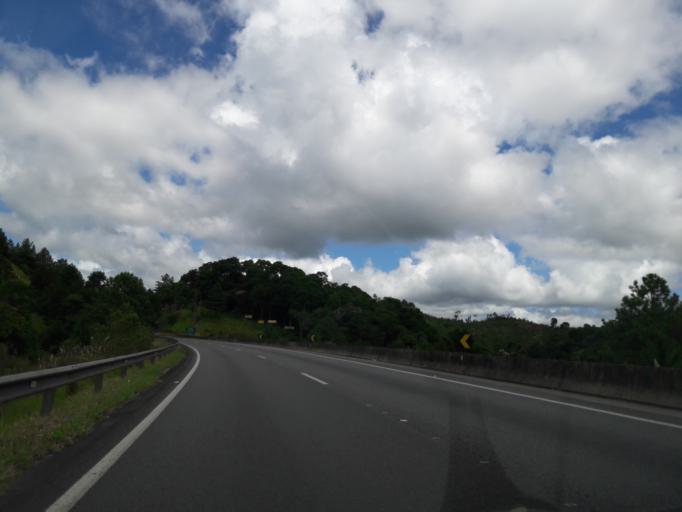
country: BR
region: Parana
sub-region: Campina Grande Do Sul
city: Campina Grande do Sul
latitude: -25.1101
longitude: -48.8526
